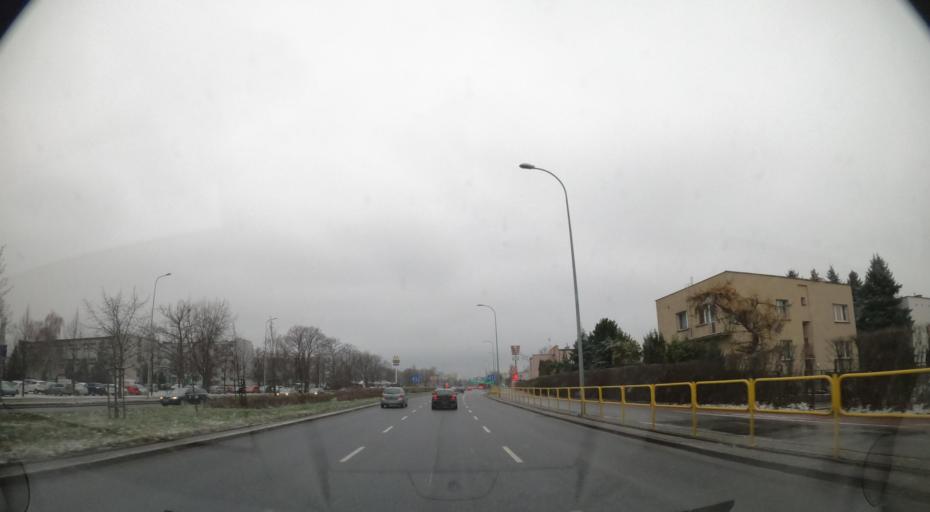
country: PL
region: Masovian Voivodeship
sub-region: Plock
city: Plock
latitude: 52.5447
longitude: 19.7128
